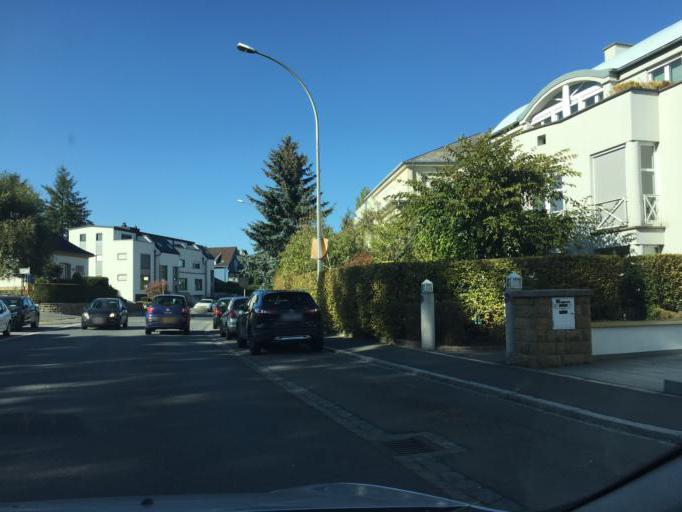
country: LU
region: Luxembourg
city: Bridel
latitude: 49.6502
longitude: 6.0834
